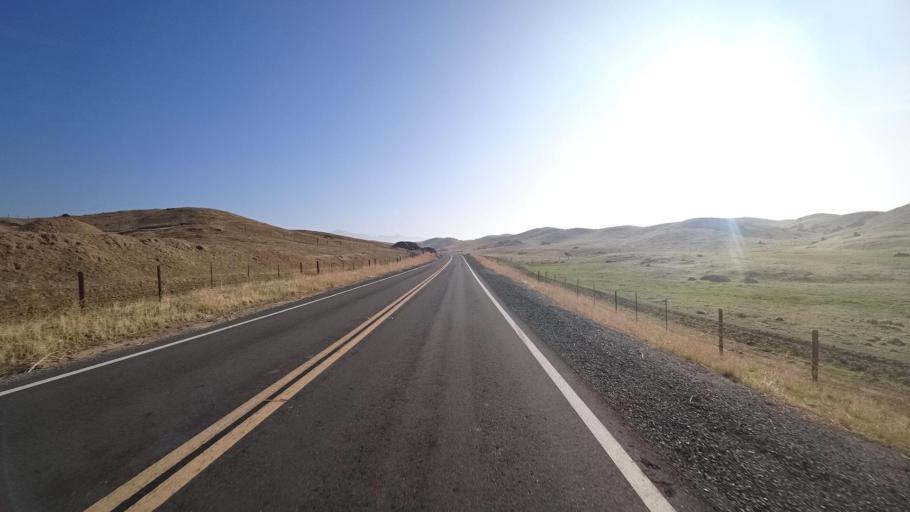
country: US
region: California
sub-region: Tulare County
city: Richgrove
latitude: 35.7419
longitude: -118.9138
